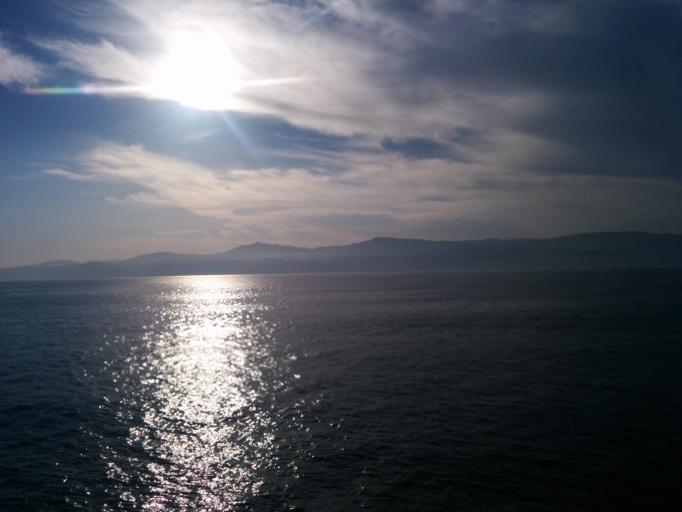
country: MA
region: Tanger-Tetouan
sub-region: Tanger-Assilah
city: Tangier
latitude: 35.8156
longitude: -5.7793
